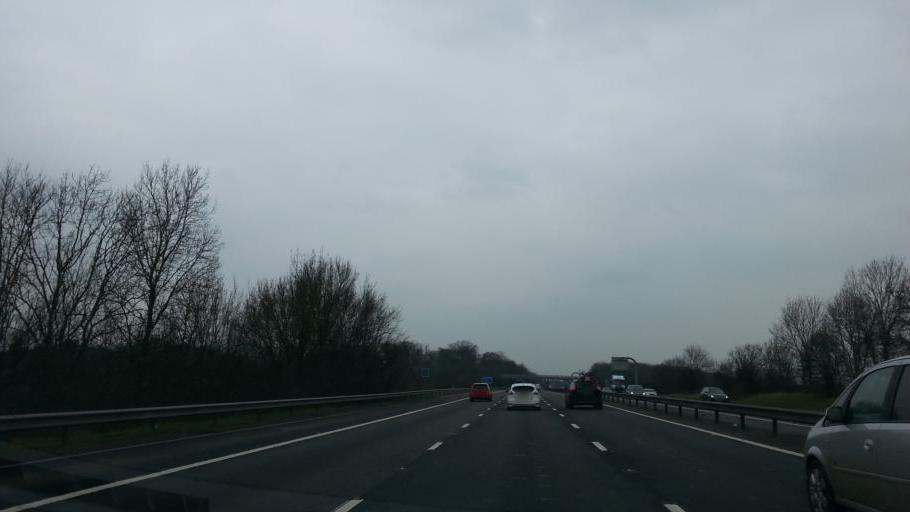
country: GB
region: England
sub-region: Gloucestershire
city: Churchdown
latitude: 51.9030
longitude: -2.1519
